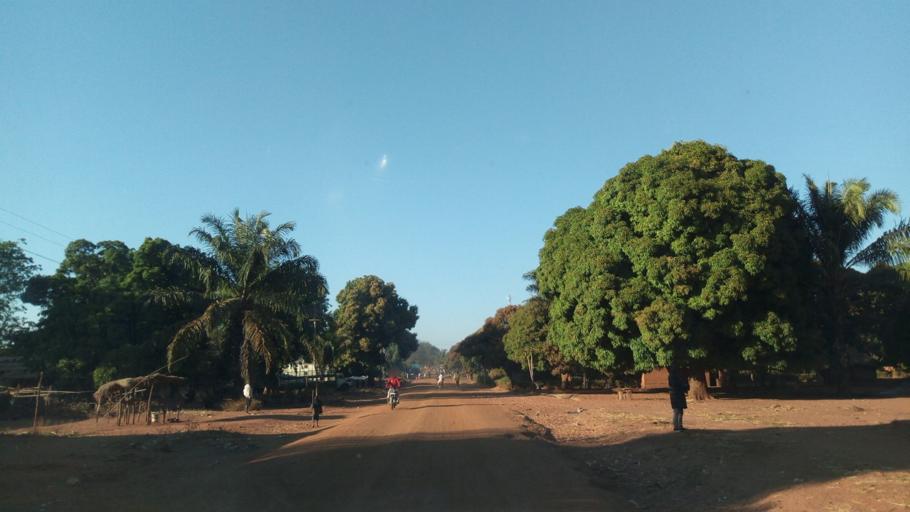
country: ZM
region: Luapula
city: Mwense
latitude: -10.3910
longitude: 28.6165
